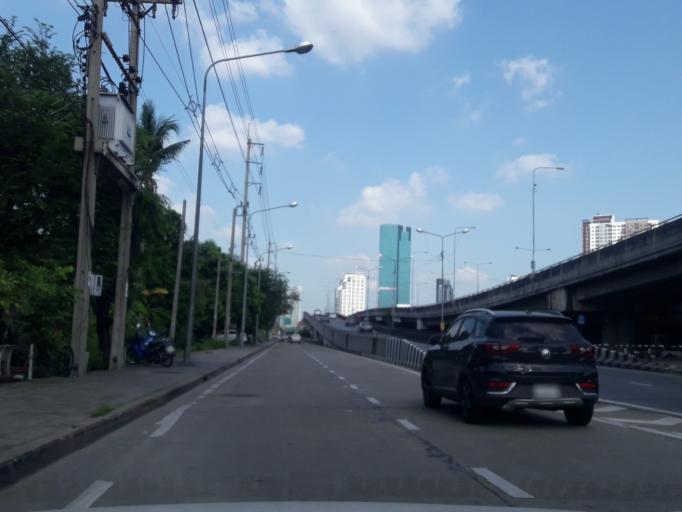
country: TH
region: Bangkok
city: Yan Nawa
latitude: 13.6941
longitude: 100.5295
